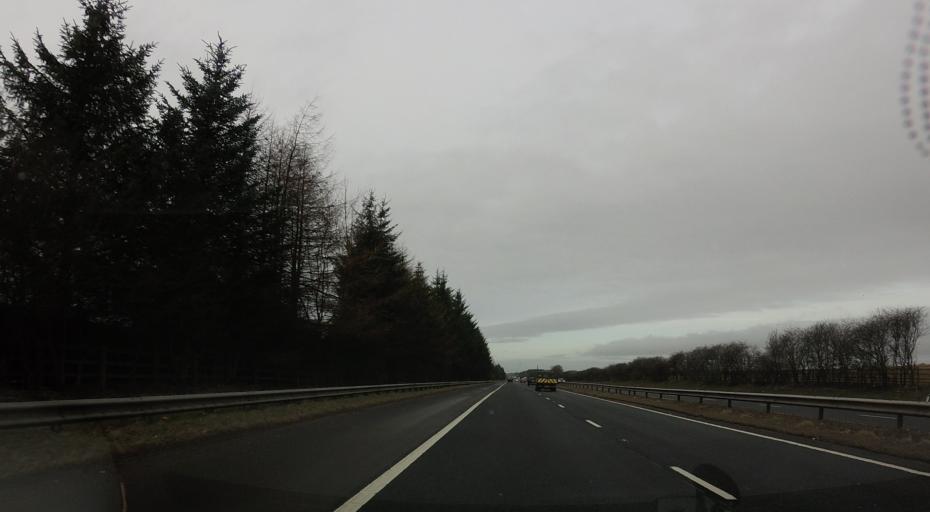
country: GB
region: Scotland
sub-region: North Lanarkshire
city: Caldercruix
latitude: 55.8467
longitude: -3.8592
